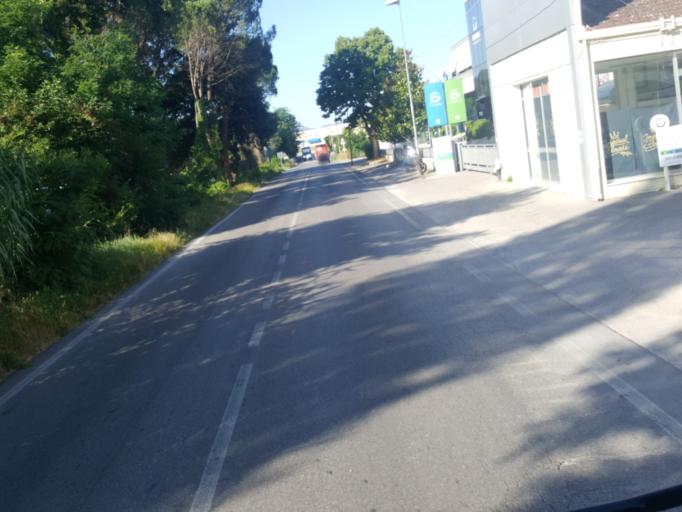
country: IT
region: The Marches
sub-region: Provincia di Pesaro e Urbino
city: Borgo Massano
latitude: 43.8293
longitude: 12.6822
